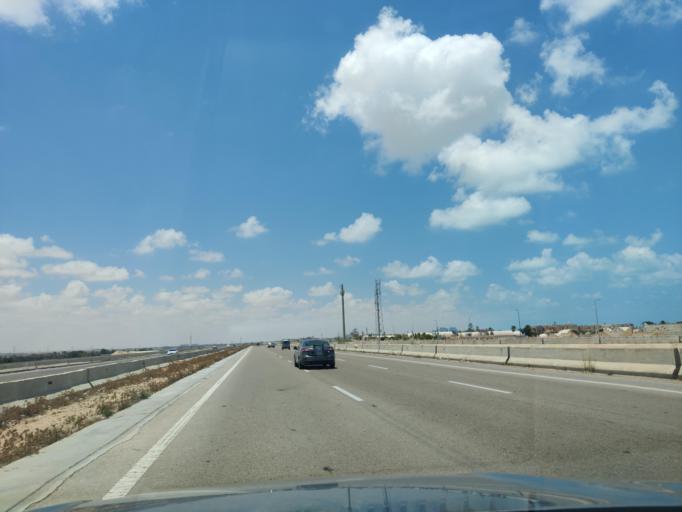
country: EG
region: Muhafazat Matruh
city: Al `Alamayn
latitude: 30.8139
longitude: 29.0463
